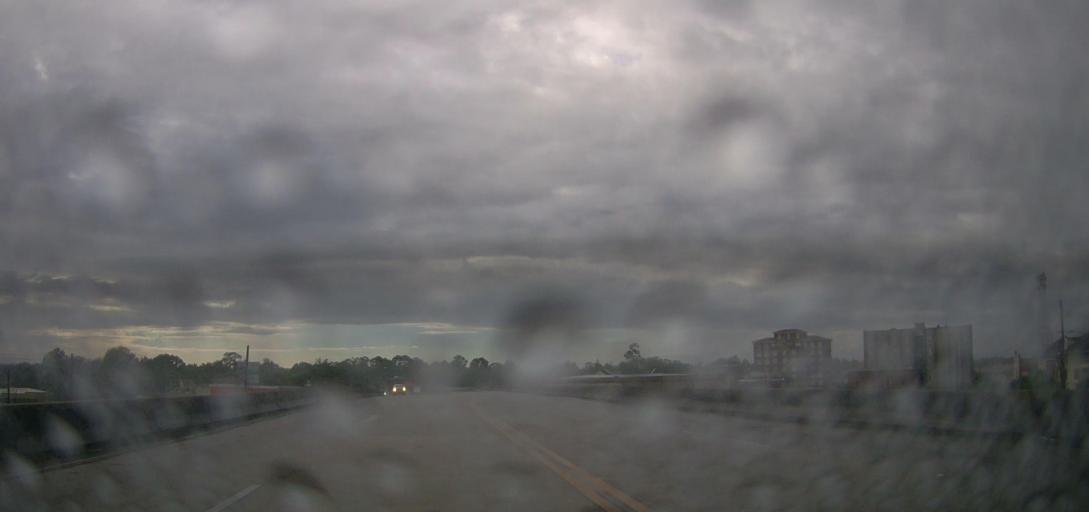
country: US
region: Georgia
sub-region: Ware County
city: Waycross
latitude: 31.2074
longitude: -82.3607
